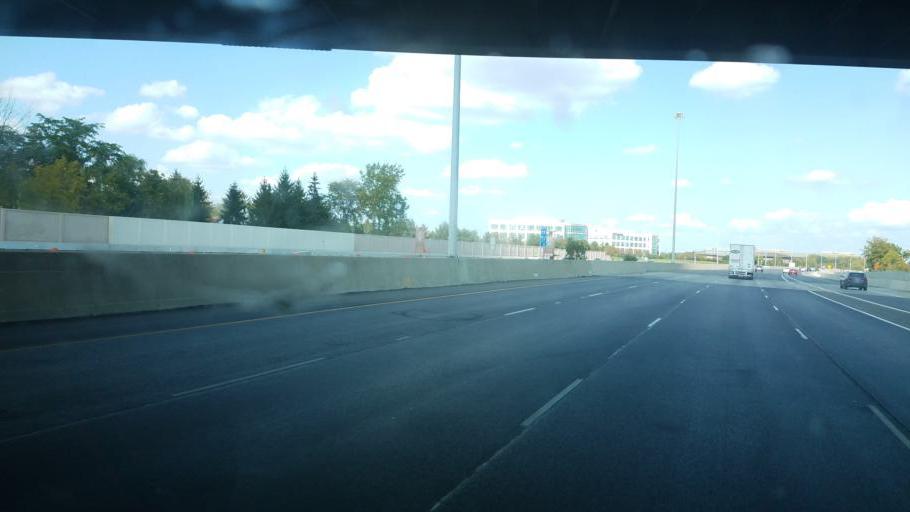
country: US
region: Ohio
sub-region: Franklin County
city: Dublin
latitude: 40.1021
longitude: -83.1311
